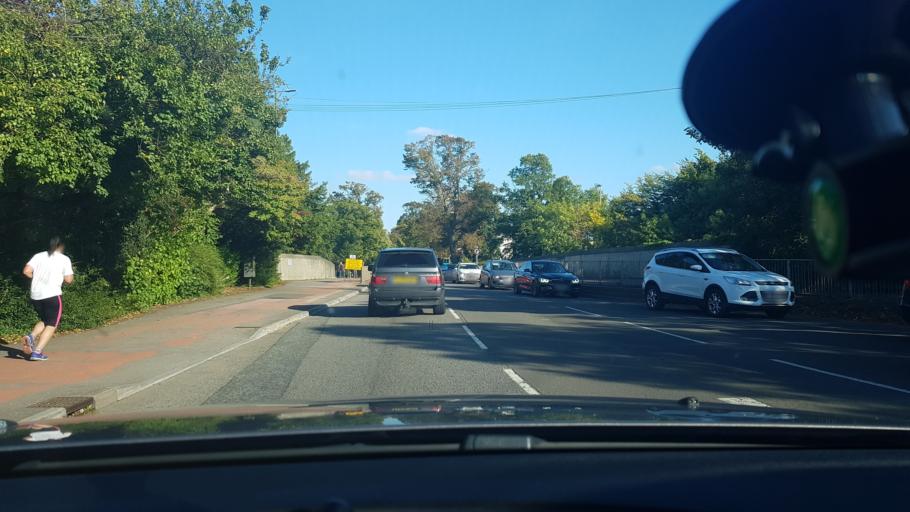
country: GB
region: England
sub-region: Gloucestershire
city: Cheltenham
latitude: 51.8950
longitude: -2.1045
